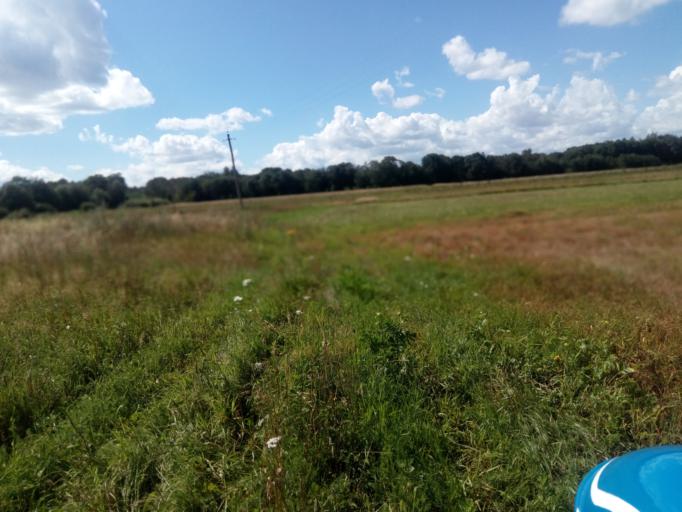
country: BY
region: Vitebsk
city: Dzisna
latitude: 55.6783
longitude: 28.3230
